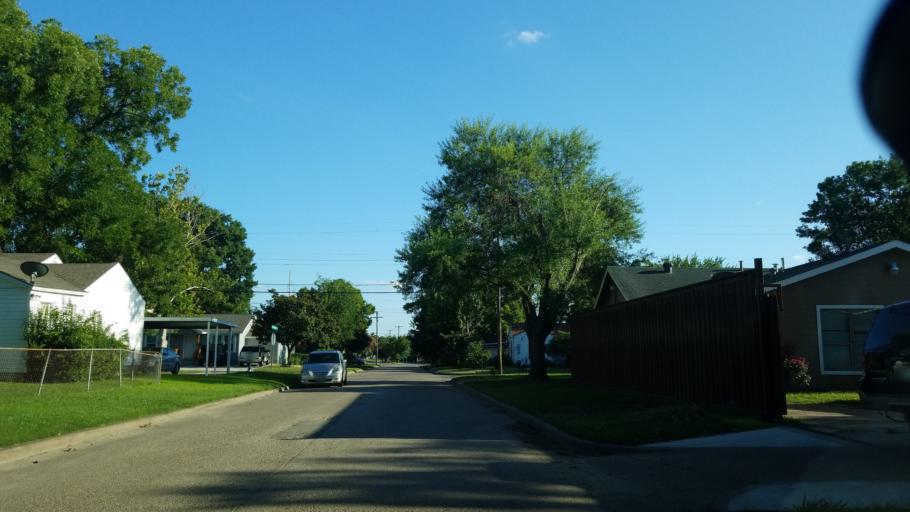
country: US
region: Texas
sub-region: Dallas County
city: Balch Springs
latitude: 32.7755
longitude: -96.7066
